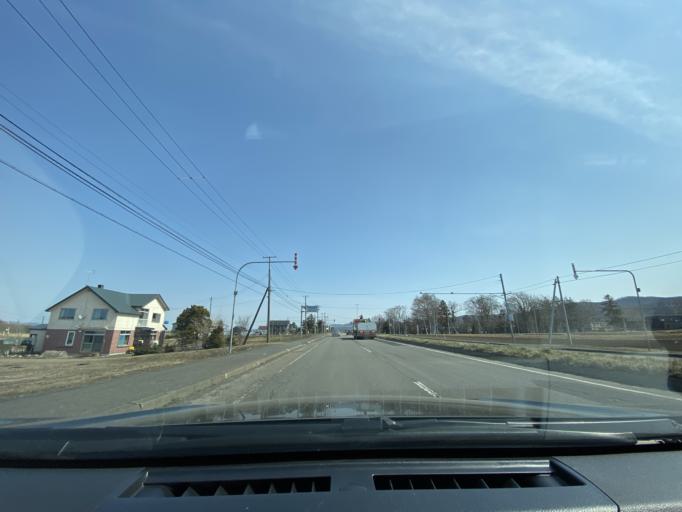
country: JP
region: Hokkaido
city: Bibai
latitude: 43.2818
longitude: 141.8352
